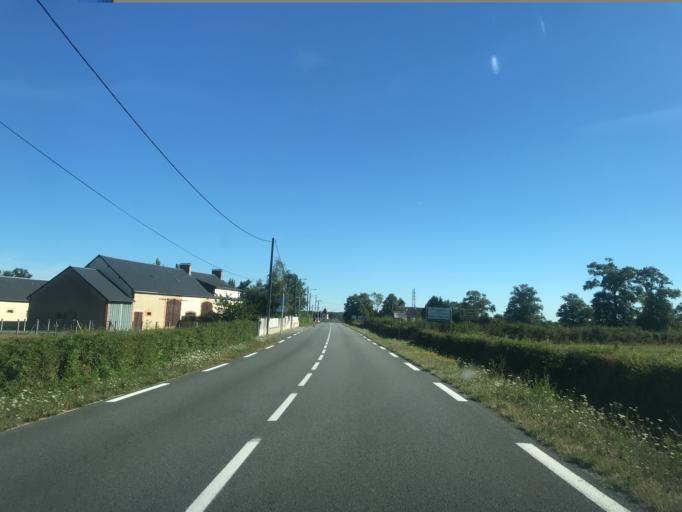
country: FR
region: Limousin
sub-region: Departement de la Creuse
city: Gouzon
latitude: 46.1813
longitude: 2.2297
